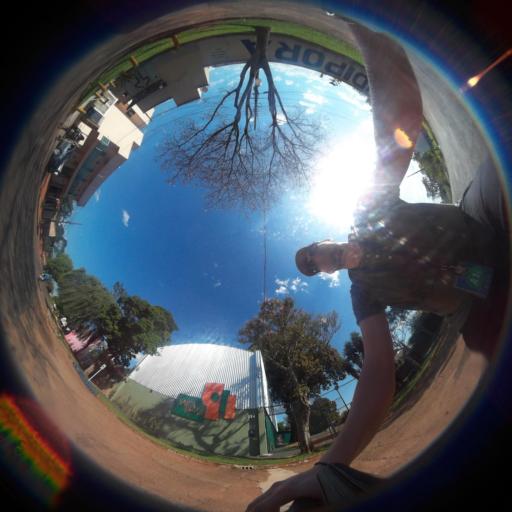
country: BR
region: Mato Grosso do Sul
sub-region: Ponta Pora
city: Ponta Pora
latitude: -22.5275
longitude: -55.7345
